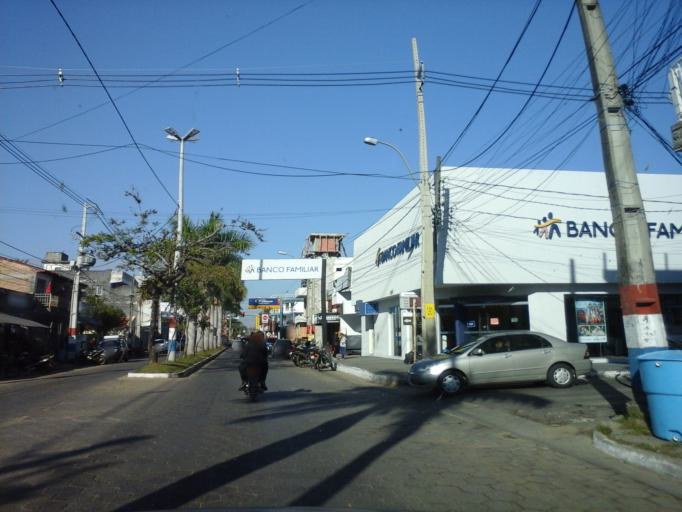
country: PY
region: Neembucu
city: Pilar
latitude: -26.8591
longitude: -58.2986
